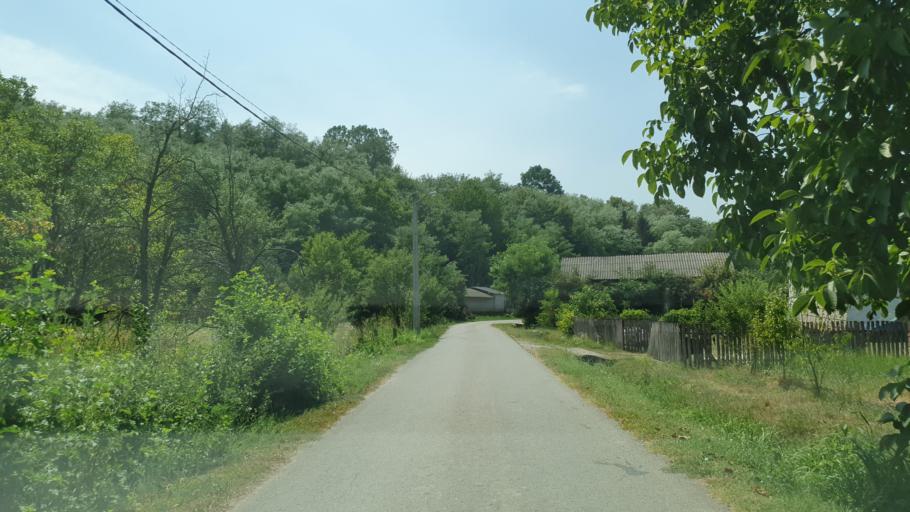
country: BA
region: Republika Srpska
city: Bijeljina
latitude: 44.7217
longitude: 19.1955
